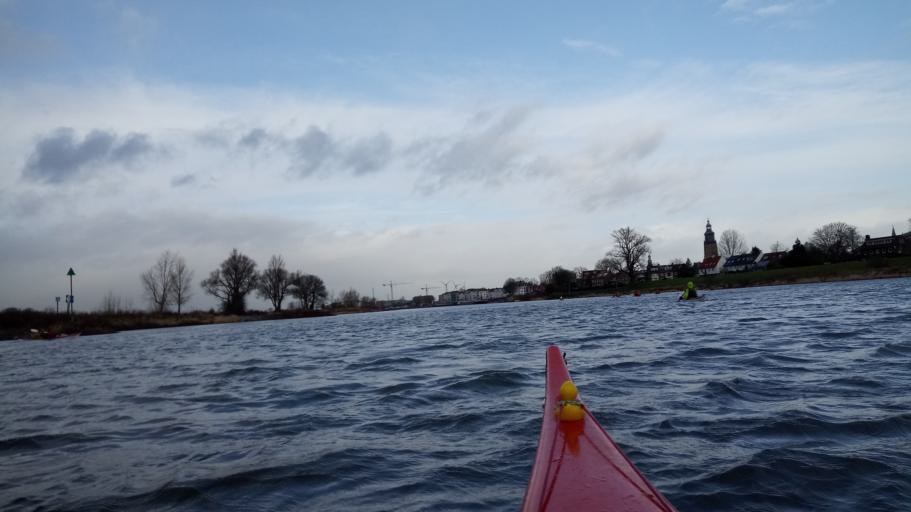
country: NL
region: Gelderland
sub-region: Gemeente Zutphen
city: Zutphen
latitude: 52.1325
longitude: 6.1910
